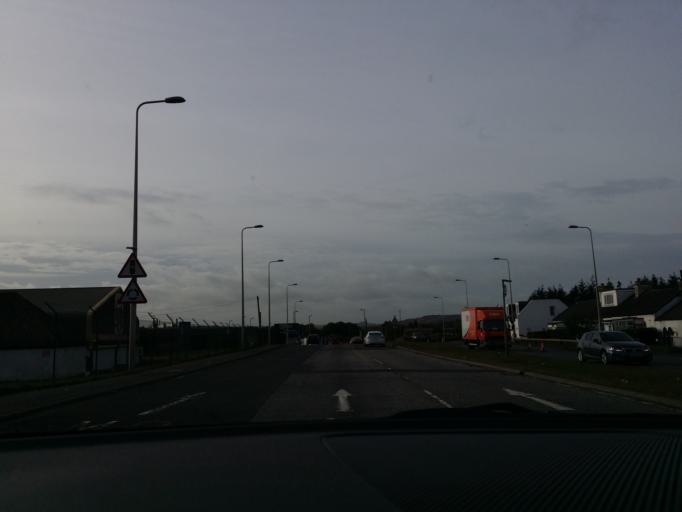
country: GB
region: Scotland
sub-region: Edinburgh
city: Newbridge
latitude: 55.9389
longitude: -3.3978
